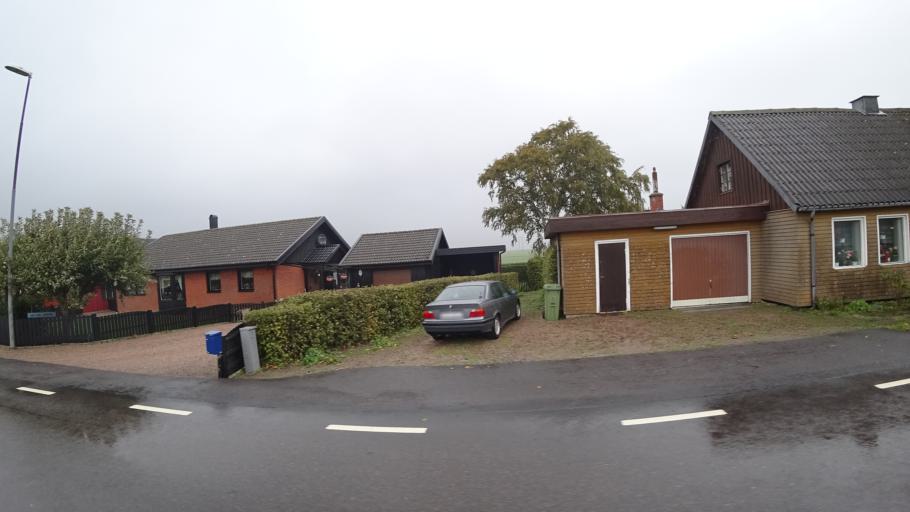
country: SE
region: Skane
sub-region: Kavlinge Kommun
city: Kaevlinge
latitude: 55.8071
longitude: 13.1509
